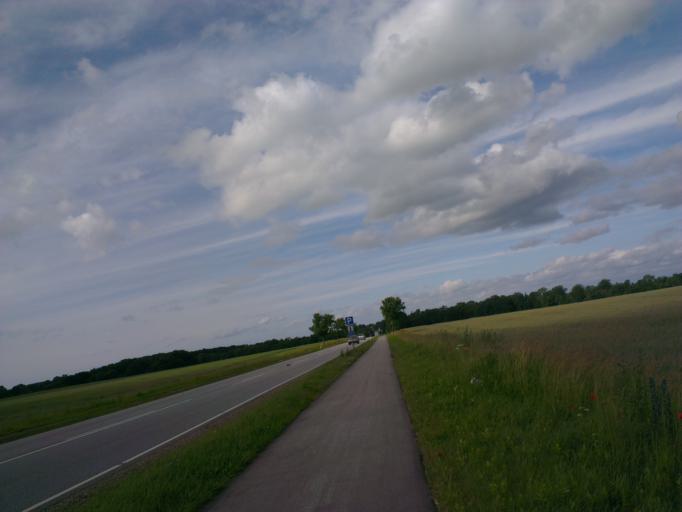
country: DK
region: Capital Region
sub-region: Frederikssund Kommune
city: Skibby
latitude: 55.7330
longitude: 11.9470
